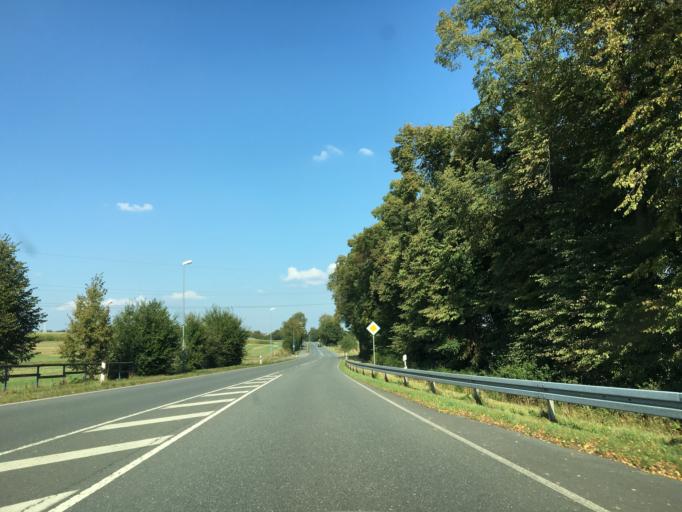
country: DE
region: Hesse
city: Frankenberg
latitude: 51.0424
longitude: 8.7900
